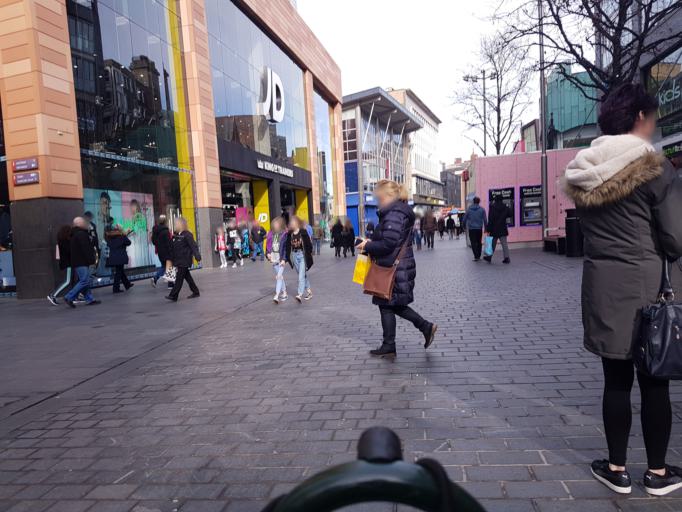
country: GB
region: England
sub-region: Liverpool
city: Liverpool
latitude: 53.4043
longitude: -2.9860
